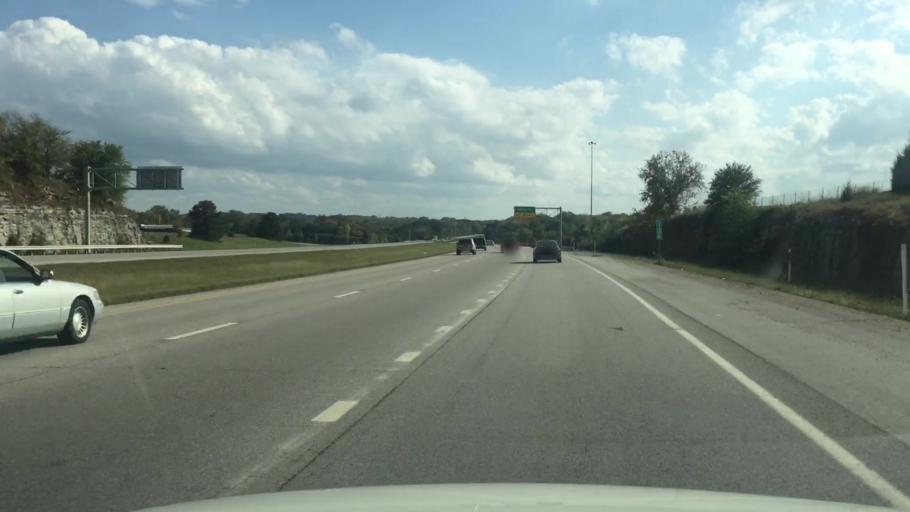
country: US
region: Kansas
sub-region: Johnson County
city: Lenexa
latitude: 38.8299
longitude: -94.6775
